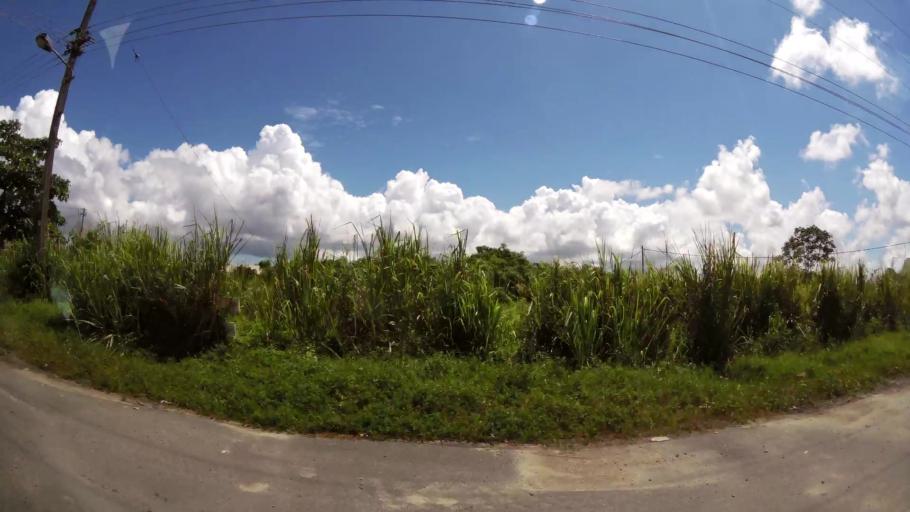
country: SR
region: Paramaribo
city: Paramaribo
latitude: 5.8652
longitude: -55.1397
